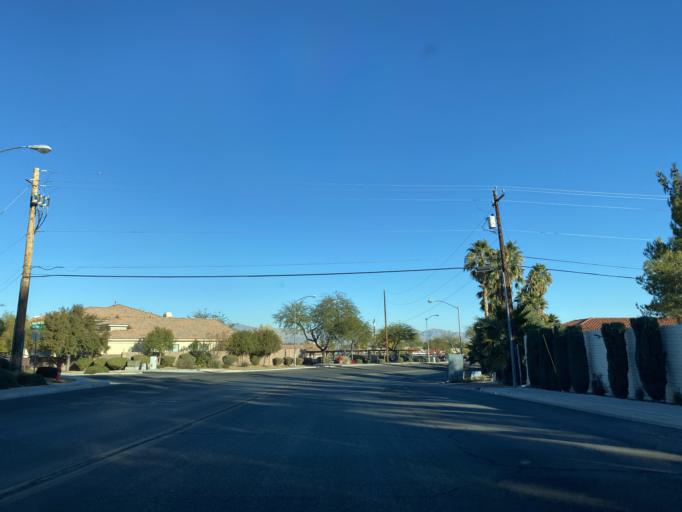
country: US
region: Nevada
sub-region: Clark County
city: Winchester
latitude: 36.1238
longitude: -115.1098
